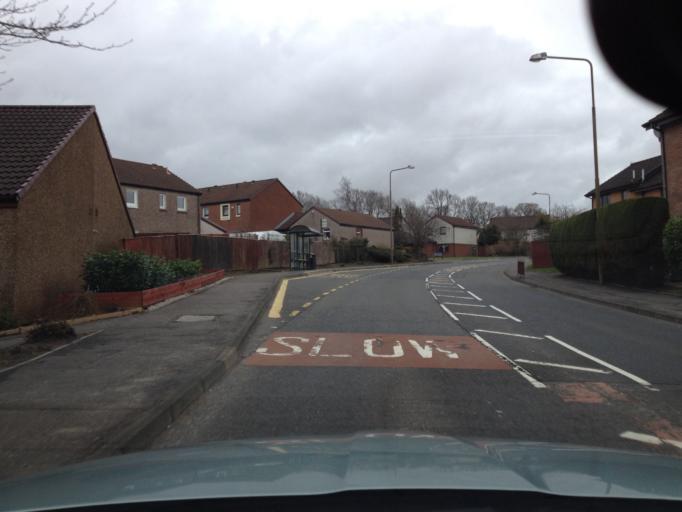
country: GB
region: Scotland
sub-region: West Lothian
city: Mid Calder
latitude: 55.8836
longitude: -3.4889
